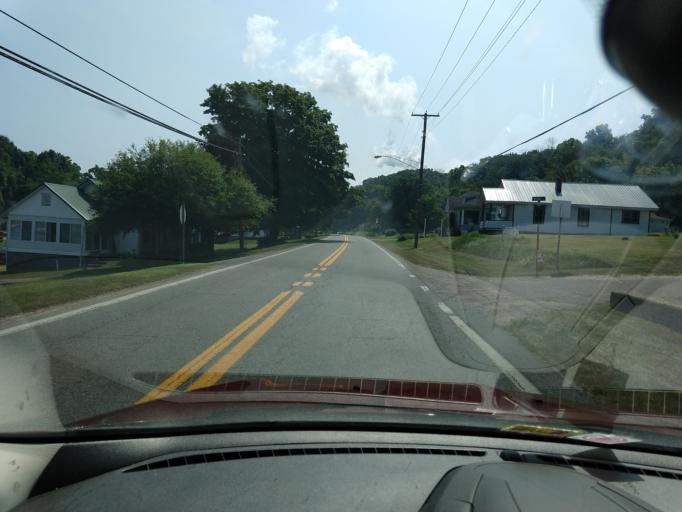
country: US
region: West Virginia
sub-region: Mason County
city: New Haven
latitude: 38.9852
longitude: -81.9654
